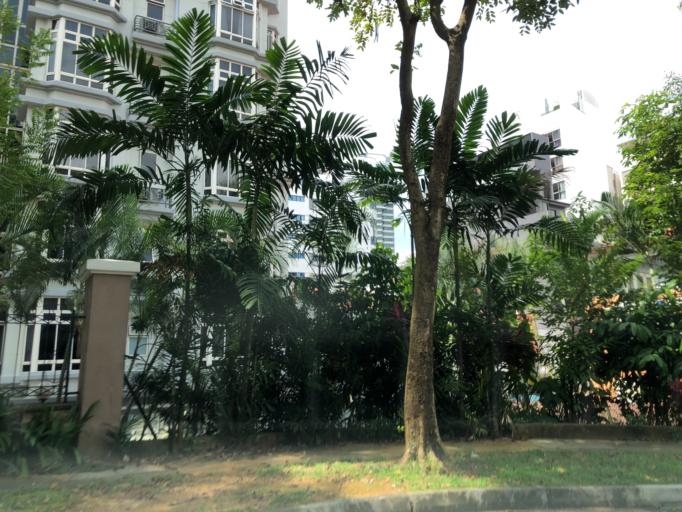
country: SG
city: Singapore
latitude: 1.2951
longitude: 103.8394
